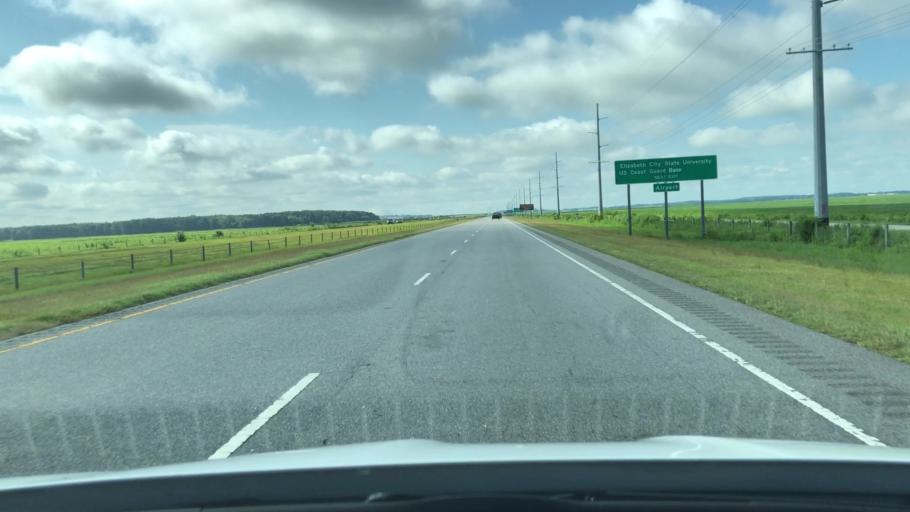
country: US
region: North Carolina
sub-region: Pasquotank County
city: Elizabeth City
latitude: 36.3148
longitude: -76.3081
